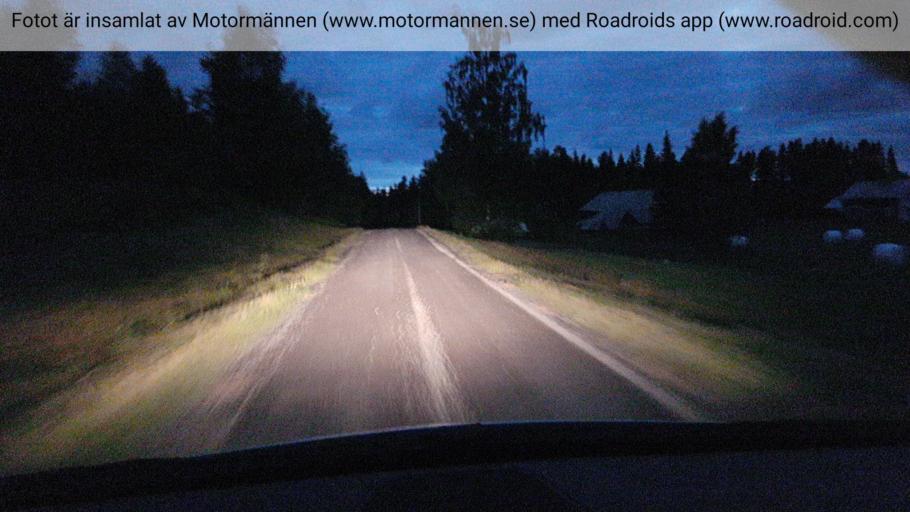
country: SE
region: Jaemtland
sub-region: OEstersunds Kommun
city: Lit
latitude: 63.3027
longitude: 15.2974
